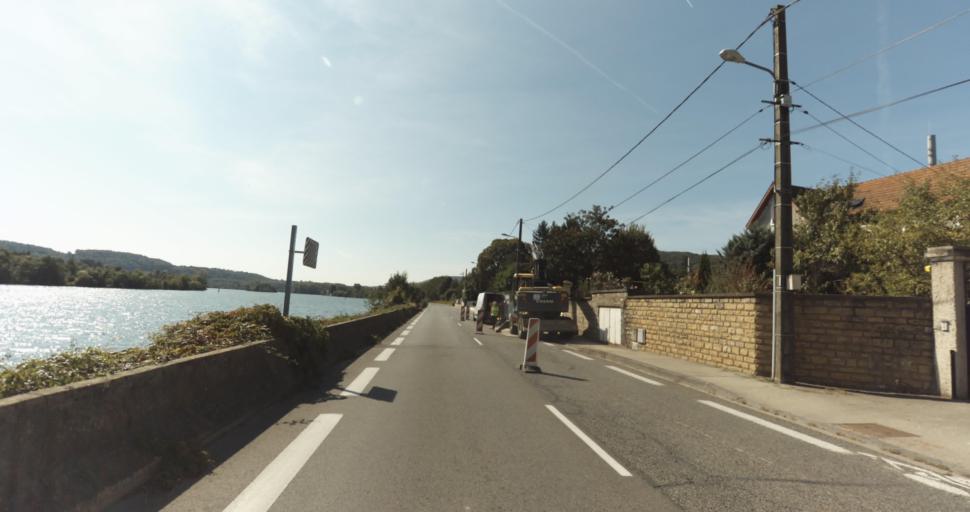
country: FR
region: Rhone-Alpes
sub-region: Departement du Rhone
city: Albigny-sur-Saone
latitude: 45.8731
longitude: 4.8350
